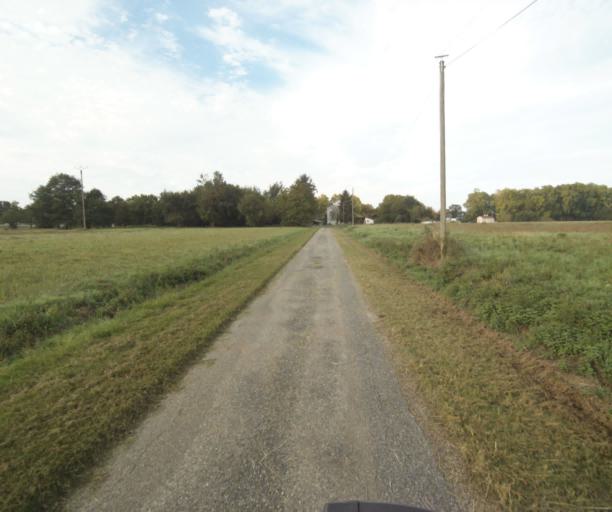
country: FR
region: Midi-Pyrenees
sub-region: Departement du Tarn-et-Garonne
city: Montech
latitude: 43.9715
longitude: 1.2297
